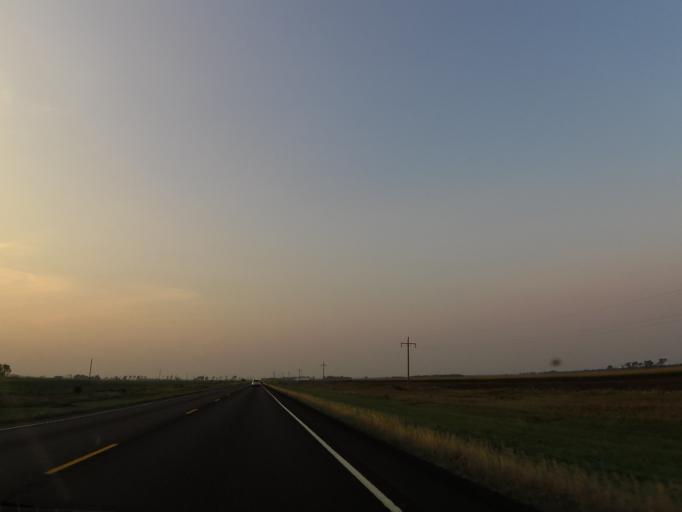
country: US
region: North Dakota
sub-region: Walsh County
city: Park River
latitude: 48.2000
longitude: -97.6225
